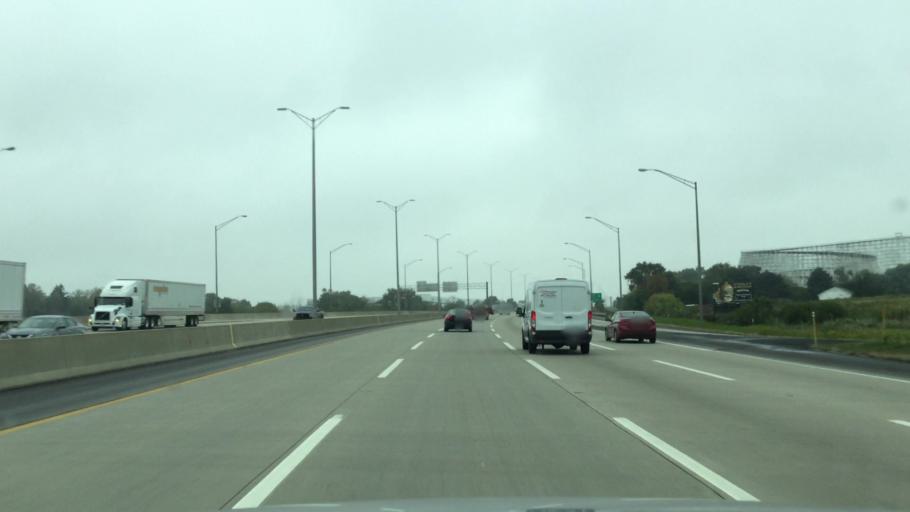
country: US
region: Illinois
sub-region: Lake County
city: Gurnee
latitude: 42.3604
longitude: -87.9369
